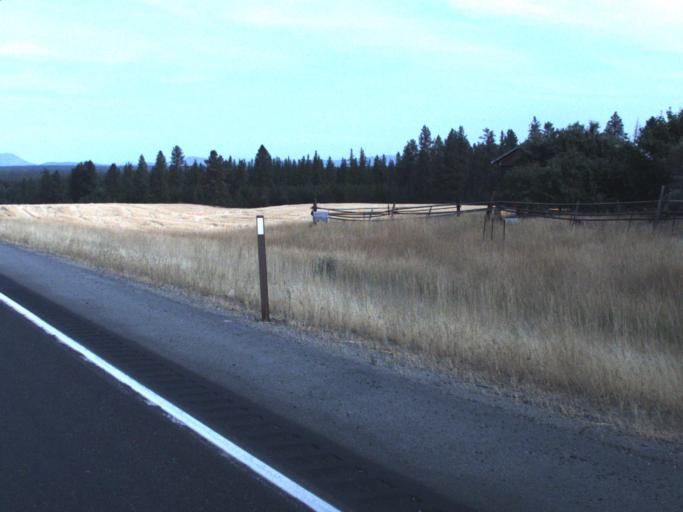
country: US
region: Washington
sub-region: Spokane County
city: Deer Park
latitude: 47.8749
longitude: -117.4221
